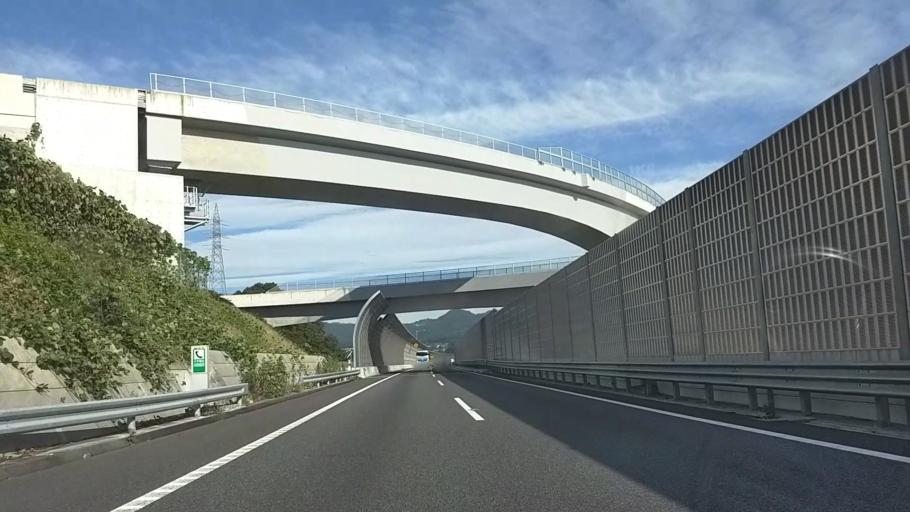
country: JP
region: Tokyo
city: Hachioji
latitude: 35.5808
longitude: 139.2938
